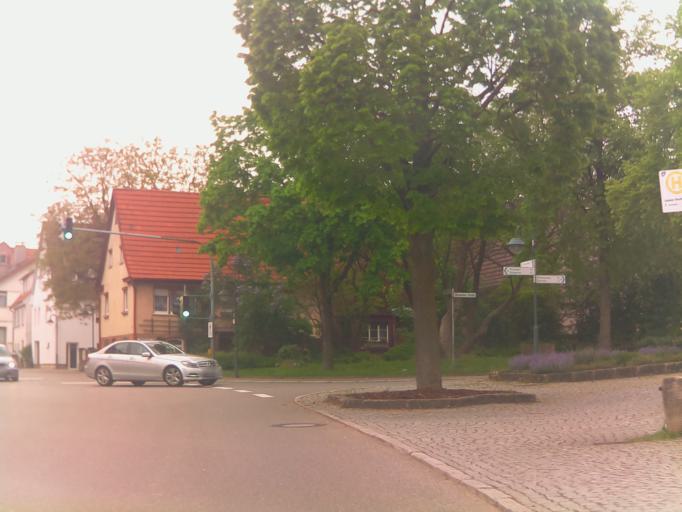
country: DE
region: Baden-Wuerttemberg
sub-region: Tuebingen Region
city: Pliezhausen
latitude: 48.5760
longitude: 9.1818
